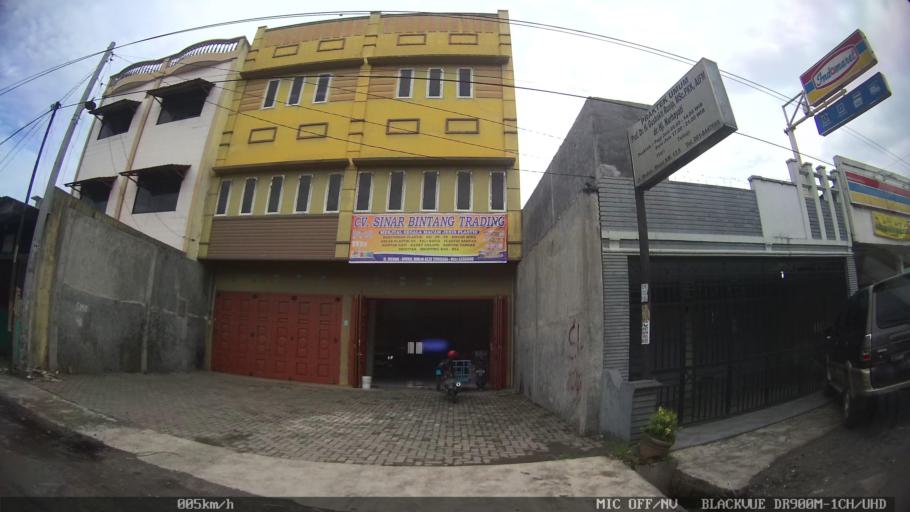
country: ID
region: North Sumatra
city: Sunggal
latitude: 3.5994
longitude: 98.5662
